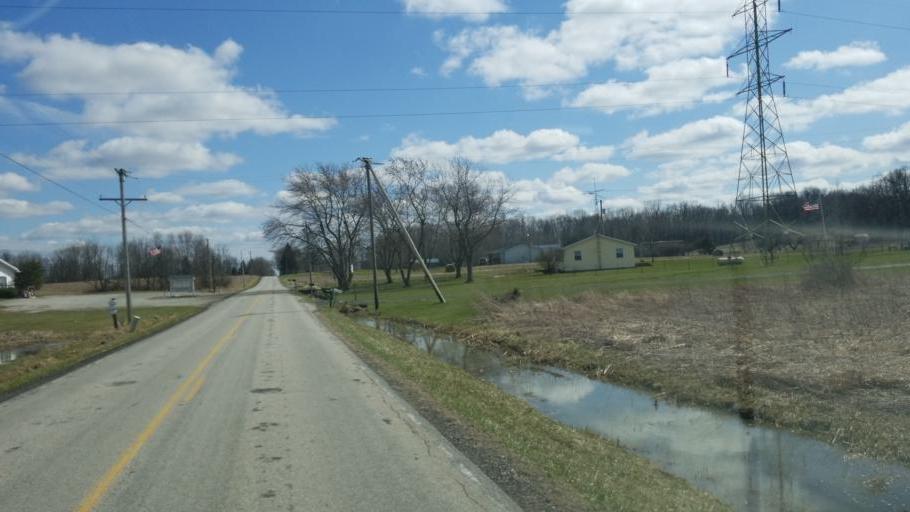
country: US
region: Ohio
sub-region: Richland County
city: Ontario
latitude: 40.8393
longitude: -82.5608
